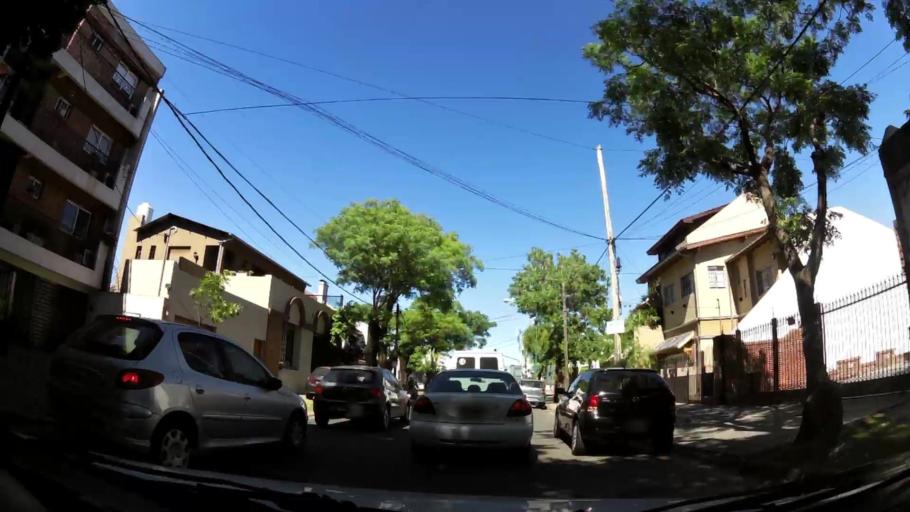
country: AR
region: Buenos Aires
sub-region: Partido de Vicente Lopez
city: Olivos
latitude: -34.5303
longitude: -58.5044
